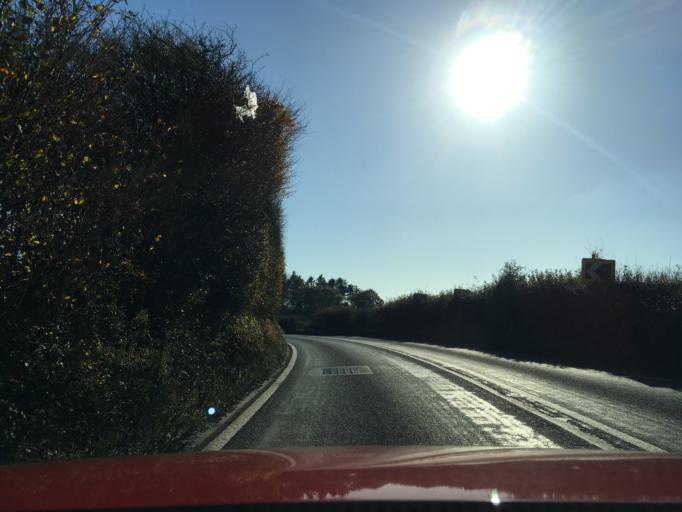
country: GB
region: England
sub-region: Somerset
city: Yeovil
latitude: 50.9035
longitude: -2.6236
